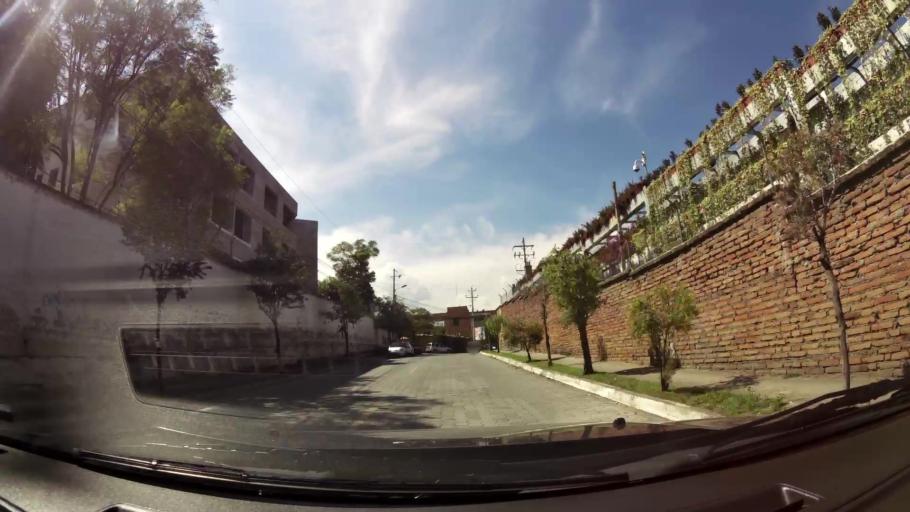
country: EC
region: Pichincha
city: Quito
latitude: -0.2050
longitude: -78.4227
